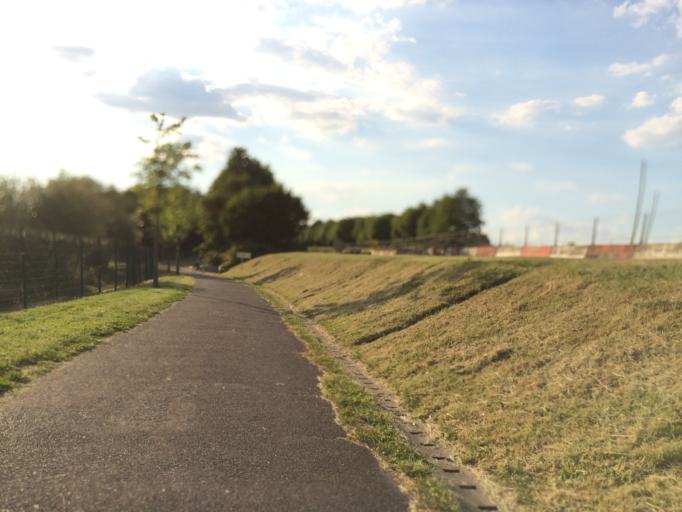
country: FR
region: Ile-de-France
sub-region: Departement de l'Essonne
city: Courcouronnes
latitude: 48.6179
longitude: 2.4203
